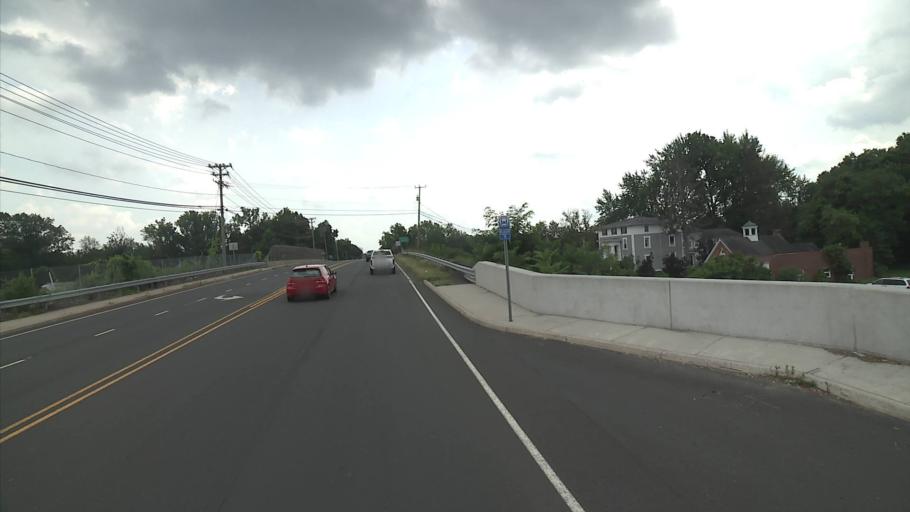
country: US
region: Connecticut
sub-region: Hartford County
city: Newington
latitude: 41.7159
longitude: -72.7373
